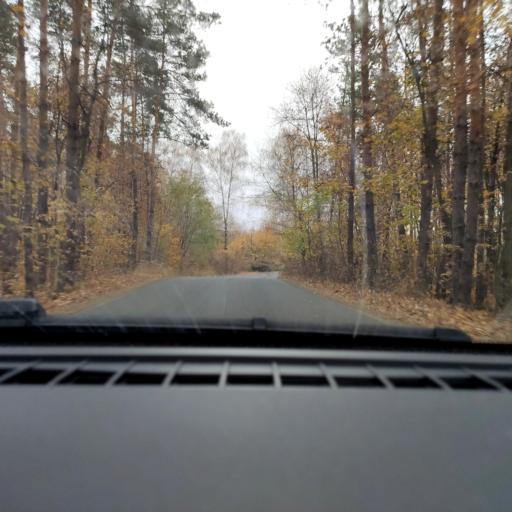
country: RU
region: Voronezj
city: Somovo
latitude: 51.6871
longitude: 39.2993
